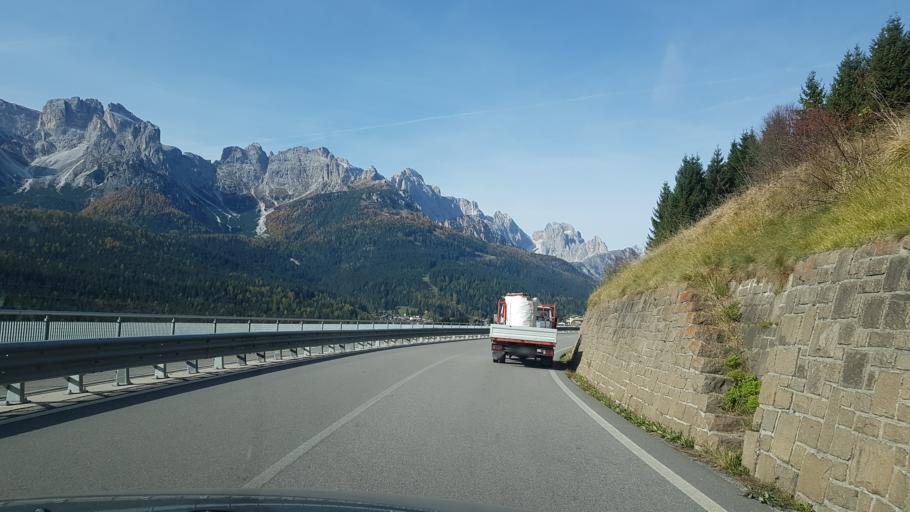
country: IT
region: Veneto
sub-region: Provincia di Belluno
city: Candide
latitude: 46.5932
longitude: 12.5033
